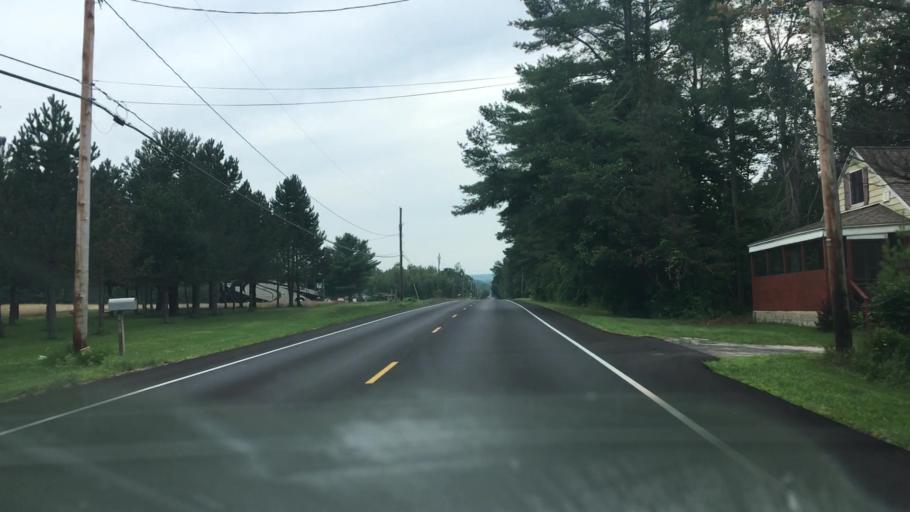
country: US
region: New York
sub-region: Clinton County
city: Plattsburgh West
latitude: 44.6519
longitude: -73.5240
